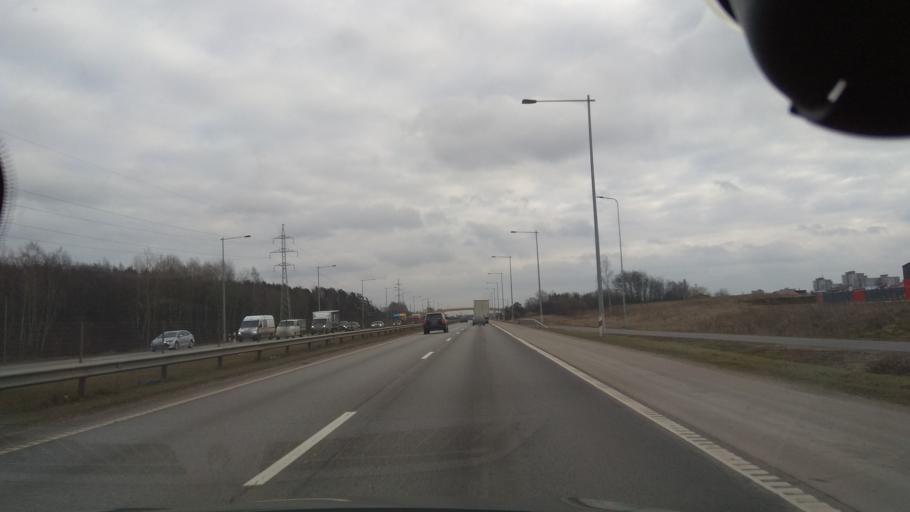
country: LT
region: Kauno apskritis
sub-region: Kaunas
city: Eiguliai
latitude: 54.9351
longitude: 23.9518
